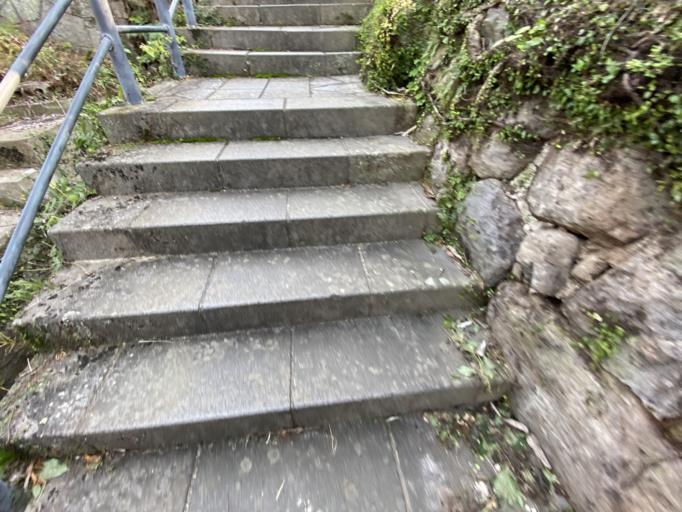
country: JP
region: Nagasaki
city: Nagasaki-shi
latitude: 32.7493
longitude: 129.8860
